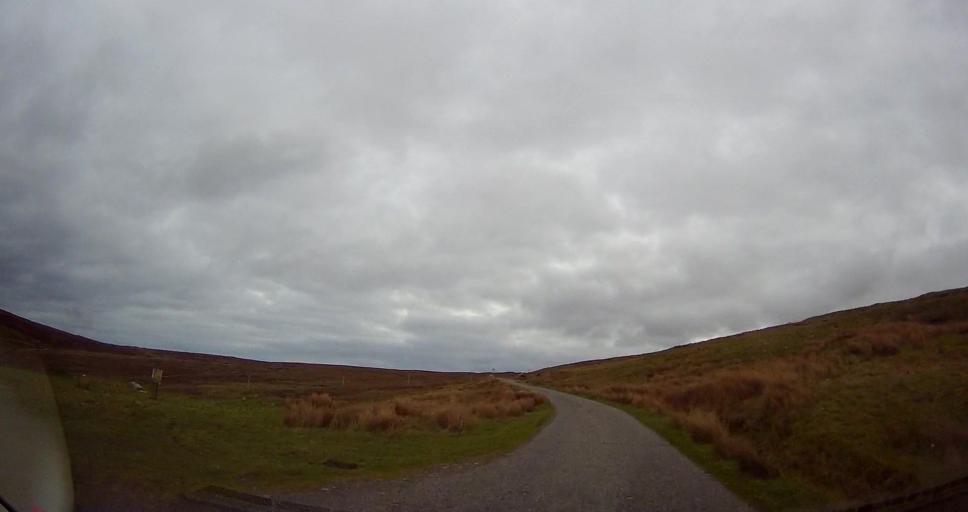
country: GB
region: Scotland
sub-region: Shetland Islands
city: Shetland
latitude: 60.5905
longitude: -1.0690
